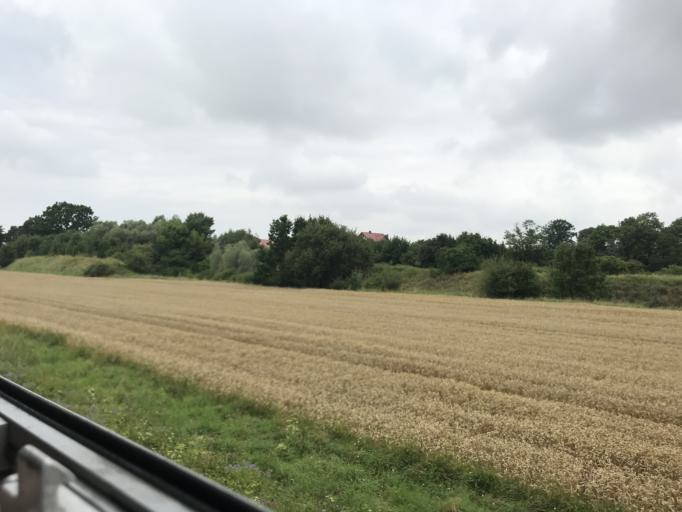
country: PL
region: Pomeranian Voivodeship
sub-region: Powiat malborski
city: Malbork
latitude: 54.0335
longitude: 19.0866
